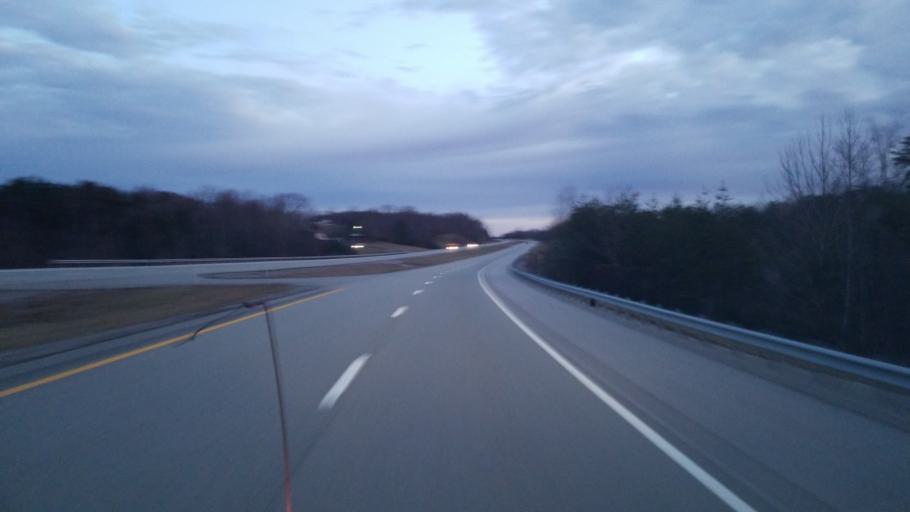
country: US
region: Tennessee
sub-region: Van Buren County
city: Spencer
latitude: 35.6967
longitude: -85.4809
